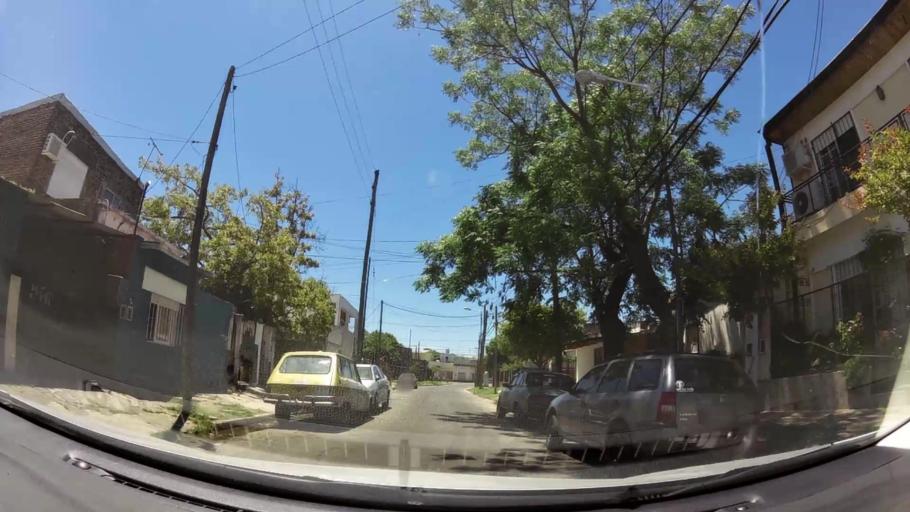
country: AR
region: Buenos Aires
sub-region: Partido de Tigre
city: Tigre
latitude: -34.4500
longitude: -58.5594
